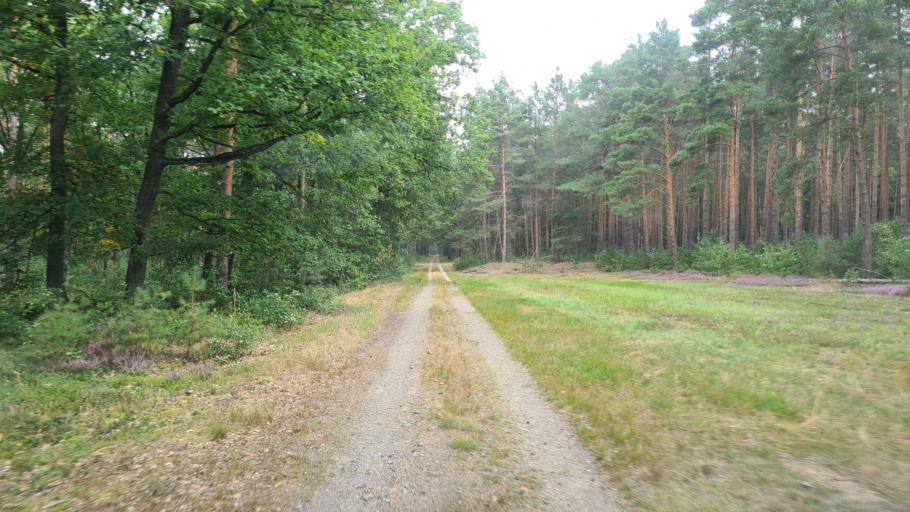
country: DE
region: Brandenburg
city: Hohenbucko
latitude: 51.7723
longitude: 13.5546
